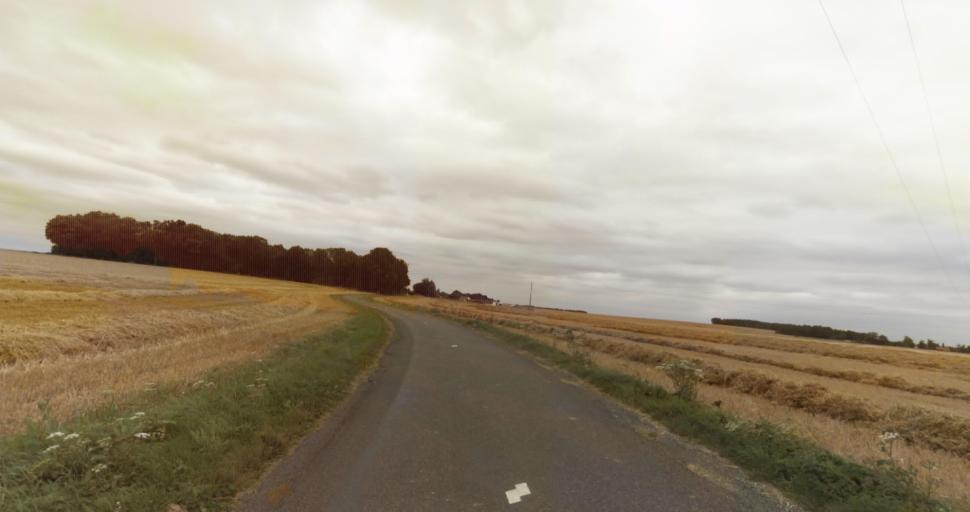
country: FR
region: Haute-Normandie
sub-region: Departement de l'Eure
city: Marcilly-sur-Eure
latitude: 48.9371
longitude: 1.2687
